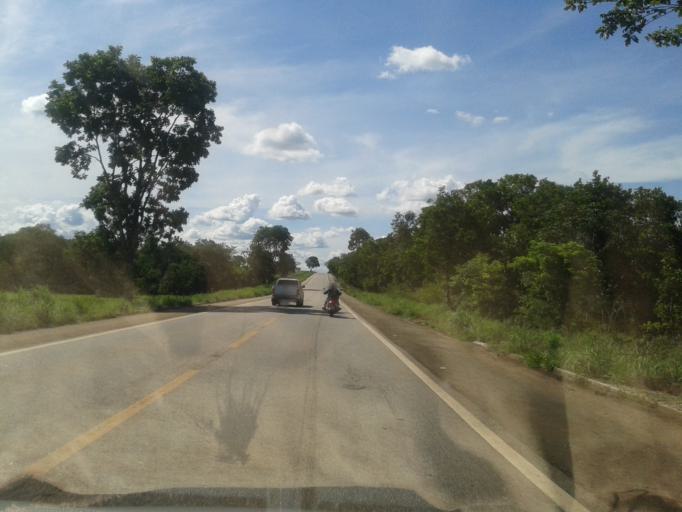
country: BR
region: Goias
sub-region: Itapirapua
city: Itapirapua
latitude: -15.3016
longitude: -50.4501
